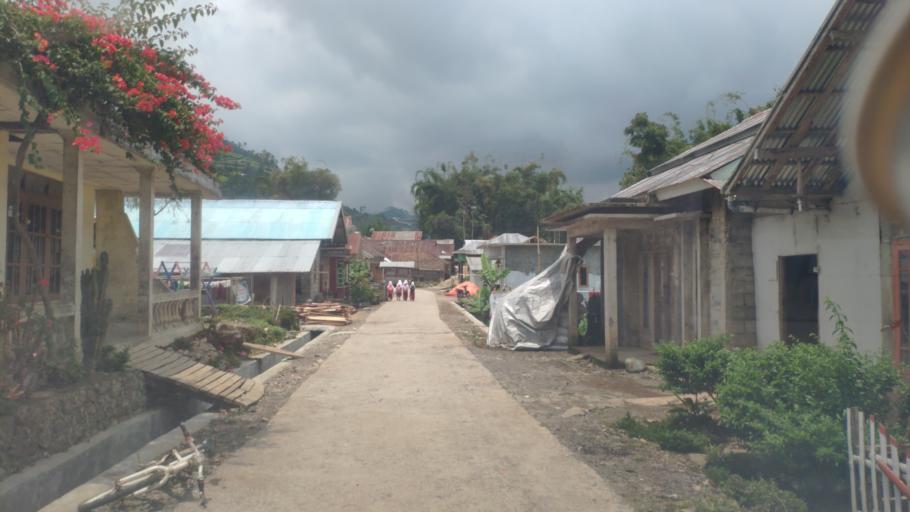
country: ID
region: Central Java
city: Wonosobo
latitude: -7.2130
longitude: 109.7542
